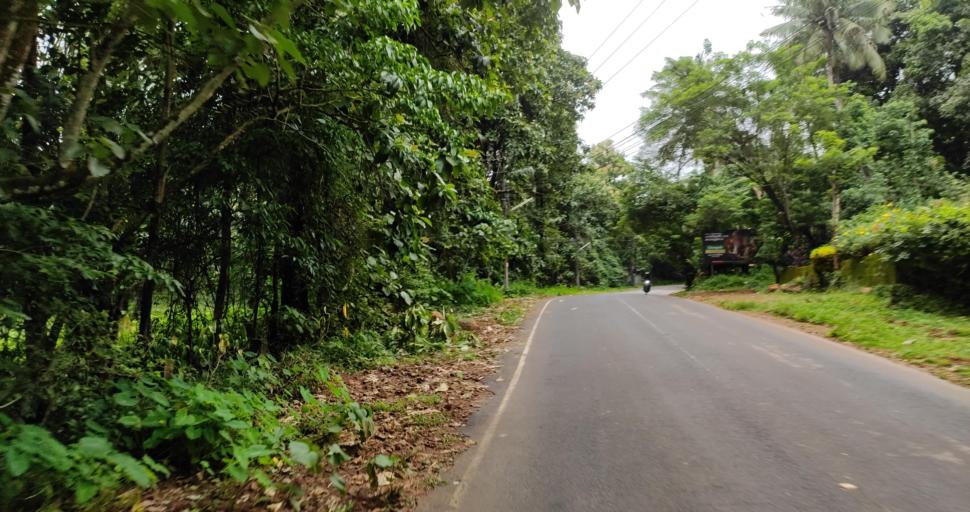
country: IN
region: Kerala
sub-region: Ernakulam
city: Angamali
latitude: 10.2909
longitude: 76.5025
